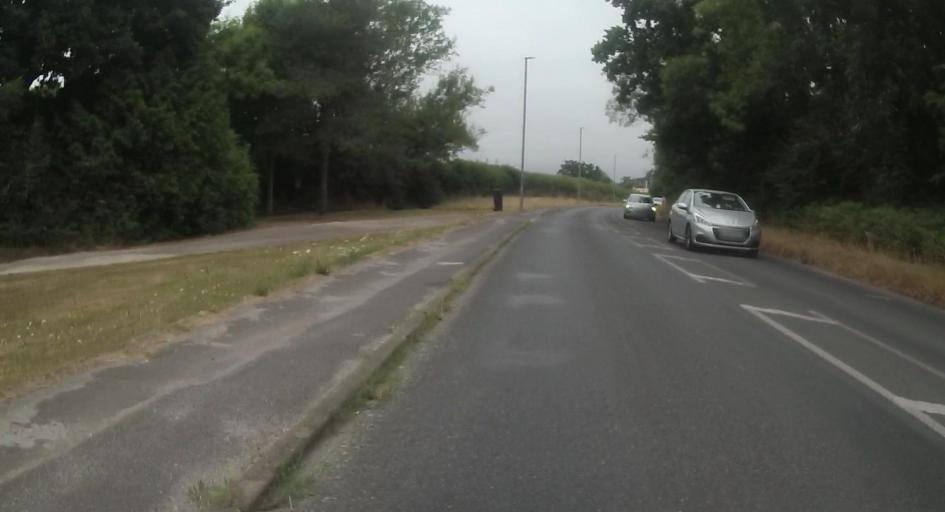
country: GB
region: England
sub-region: Dorset
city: Wareham
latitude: 50.6731
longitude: -2.1076
